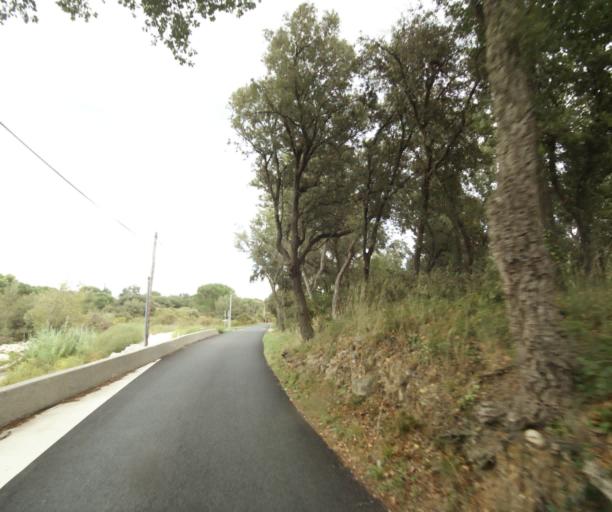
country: FR
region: Languedoc-Roussillon
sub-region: Departement des Pyrenees-Orientales
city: Argelers
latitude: 42.5412
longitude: 3.0069
